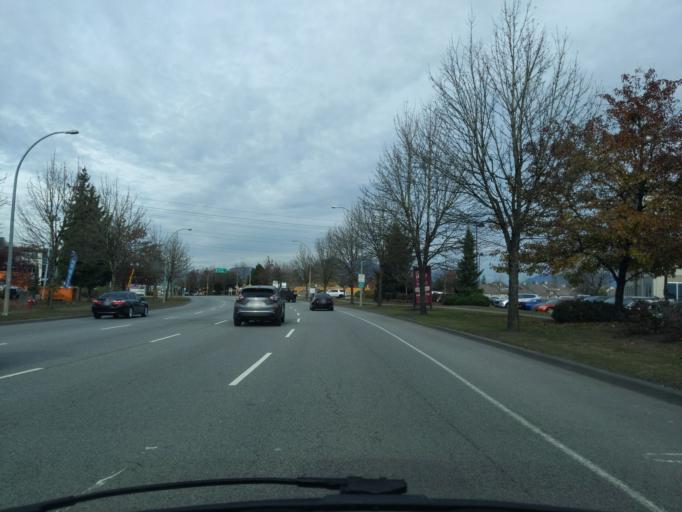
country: CA
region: British Columbia
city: Walnut Grove
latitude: 49.1745
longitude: -122.6649
